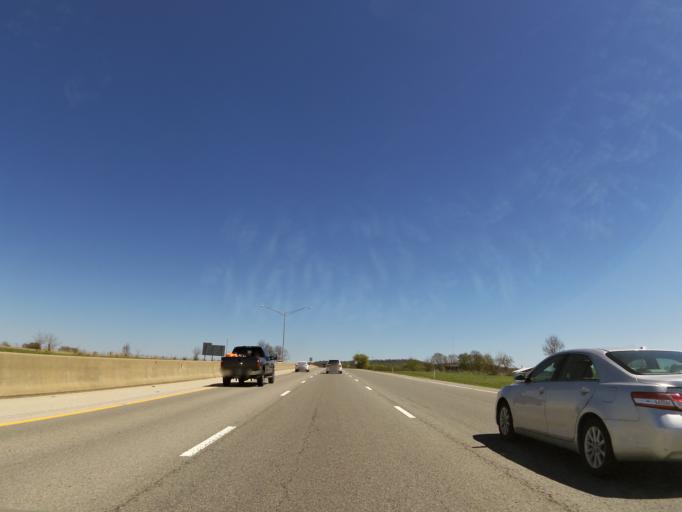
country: US
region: Kentucky
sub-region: Edmonson County
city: Brownsville
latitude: 37.0417
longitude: -86.2050
